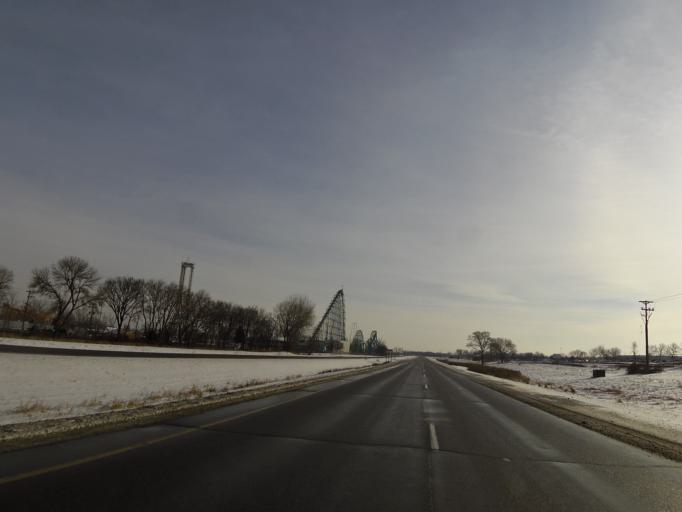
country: US
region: Minnesota
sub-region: Hennepin County
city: Eden Prairie
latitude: 44.7986
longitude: -93.4629
